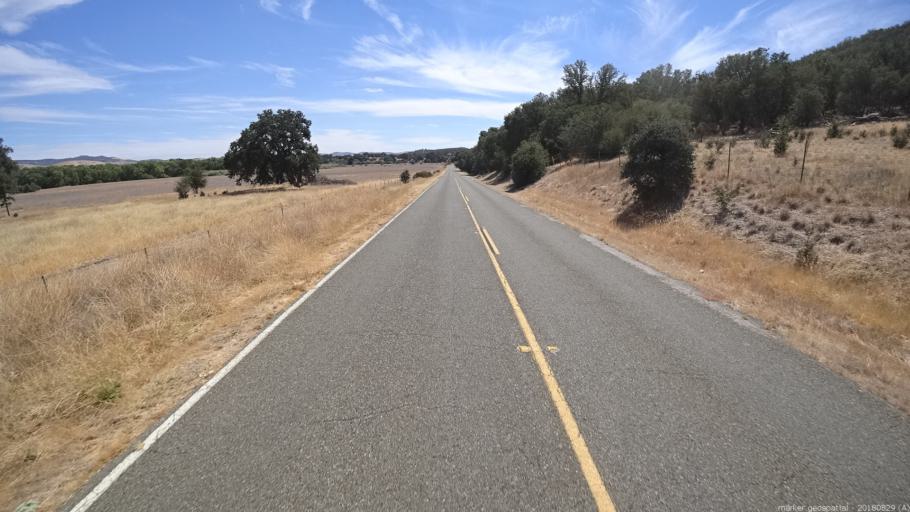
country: US
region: California
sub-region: San Luis Obispo County
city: Lake Nacimiento
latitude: 35.8889
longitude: -121.0734
